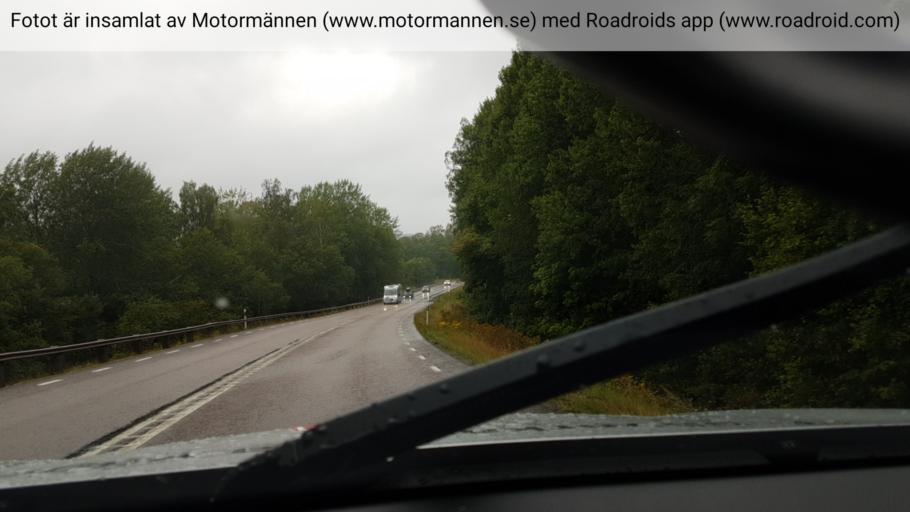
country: SE
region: Vaestra Goetaland
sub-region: Bengtsfors Kommun
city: Dals Langed
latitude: 59.0509
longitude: 12.4748
